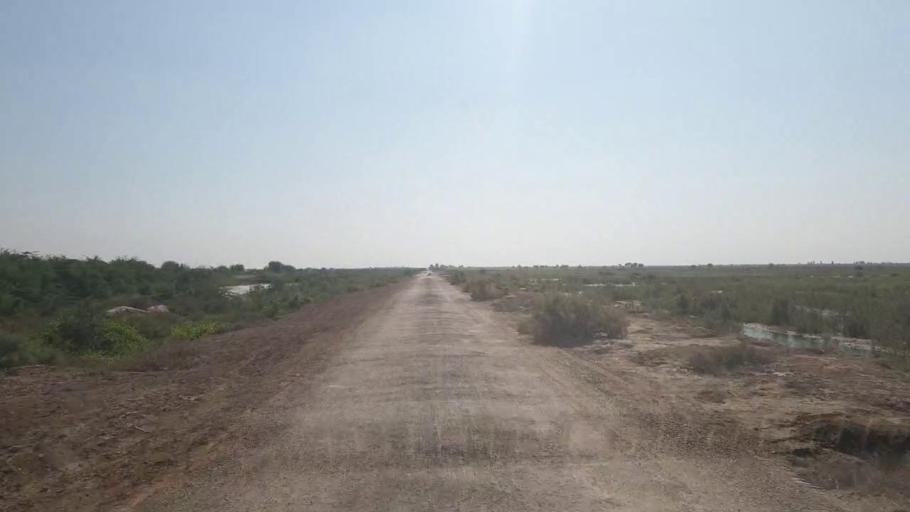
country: PK
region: Sindh
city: Tando Bago
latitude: 24.8644
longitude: 69.1643
